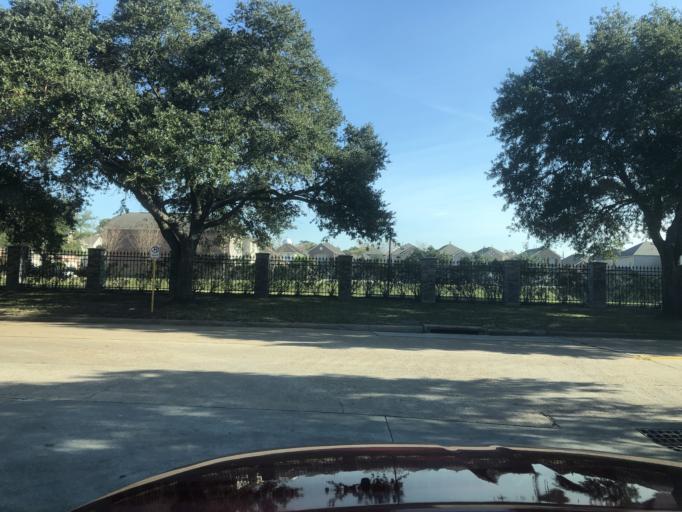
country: US
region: Texas
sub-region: Harris County
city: Spring
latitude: 30.0116
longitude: -95.4607
